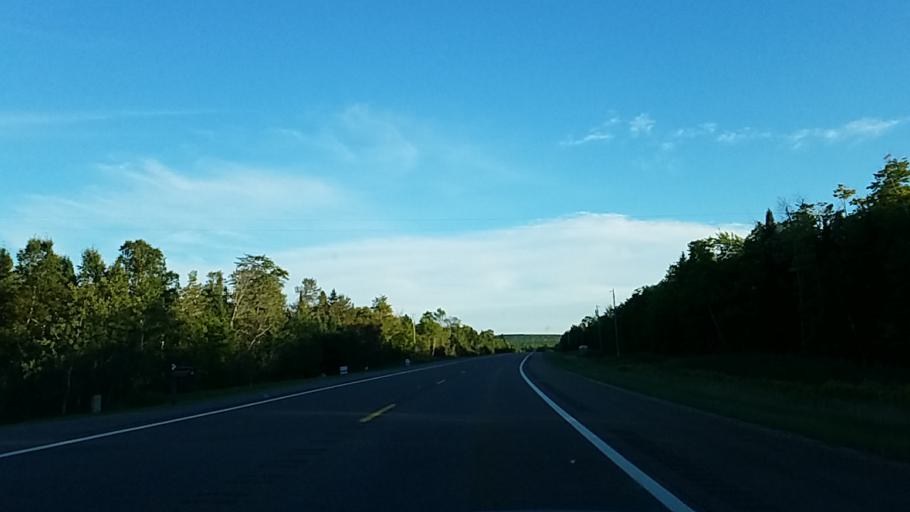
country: US
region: Michigan
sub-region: Alger County
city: Munising
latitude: 46.4540
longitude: -86.8895
